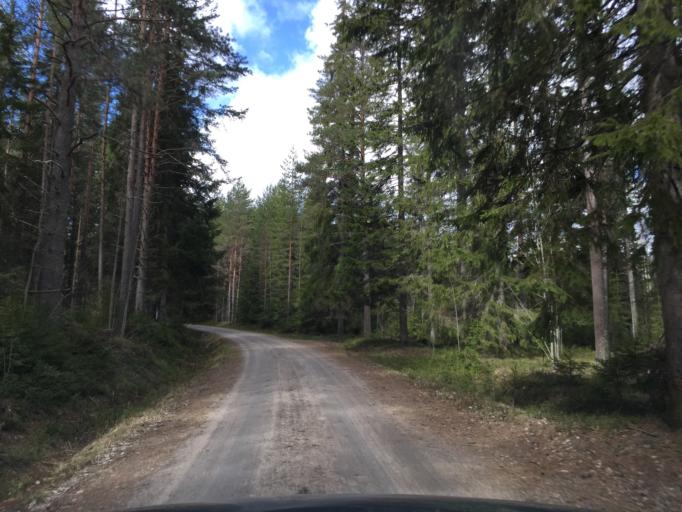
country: SE
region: Gaevleborg
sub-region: Bollnas Kommun
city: Arbra
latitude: 61.5238
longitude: 16.3166
